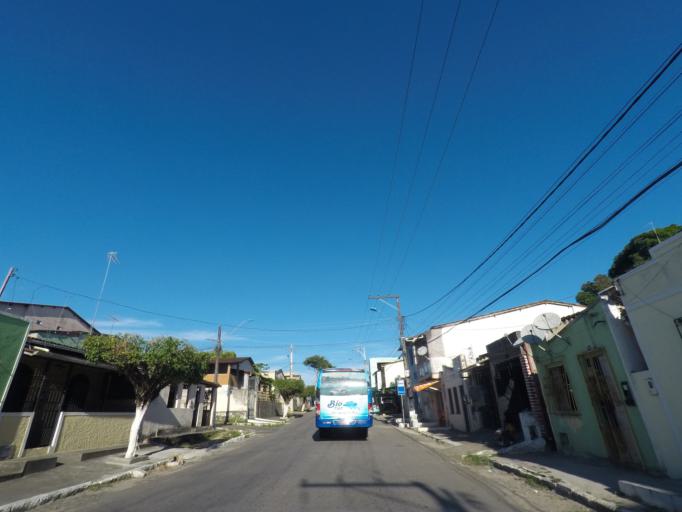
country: BR
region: Bahia
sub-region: Nazare
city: Nazare
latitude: -13.0350
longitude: -39.0172
